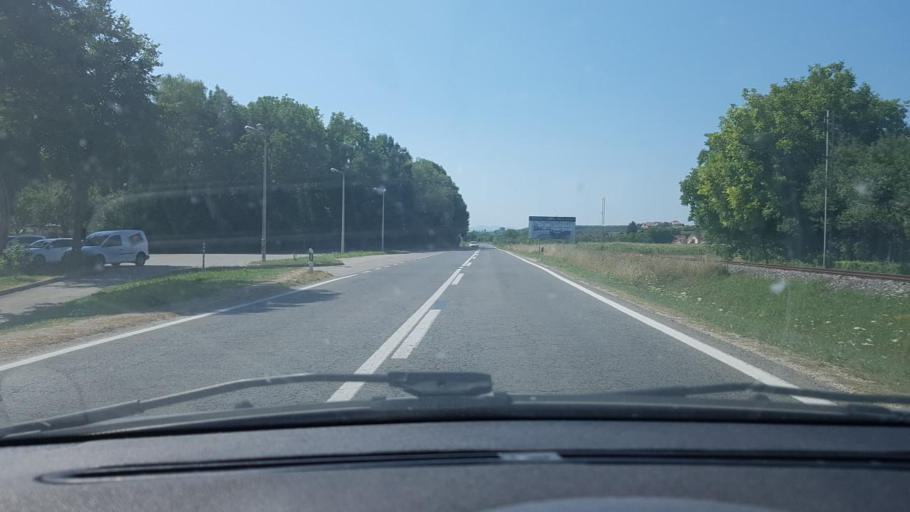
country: BA
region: Federation of Bosnia and Herzegovina
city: Bihac
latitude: 44.8014
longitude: 15.9079
